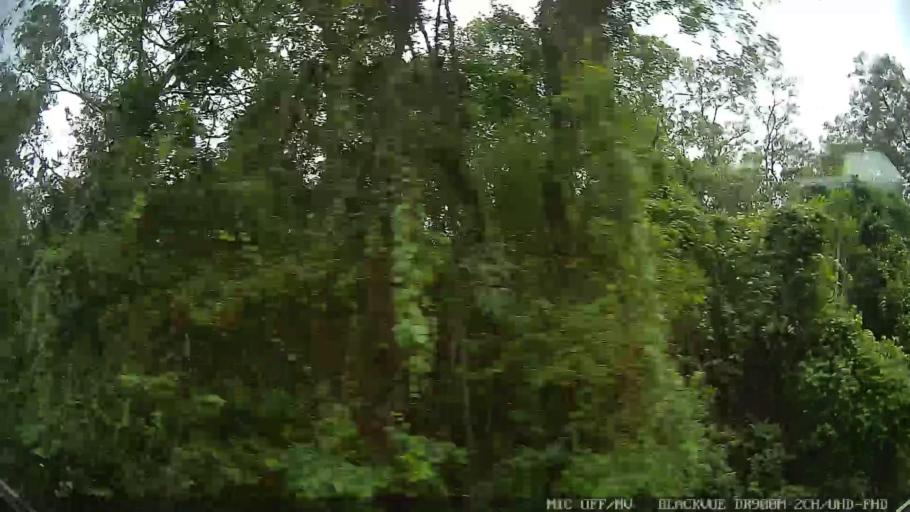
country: BR
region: Sao Paulo
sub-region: Itatiba
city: Itatiba
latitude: -23.0512
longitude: -46.8789
